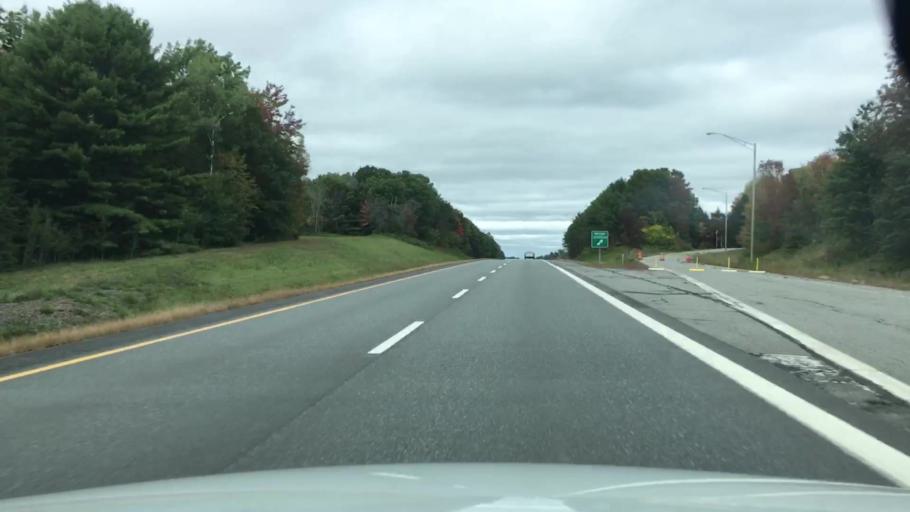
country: US
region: Maine
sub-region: Waldo County
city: Burnham
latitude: 44.7439
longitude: -69.4266
